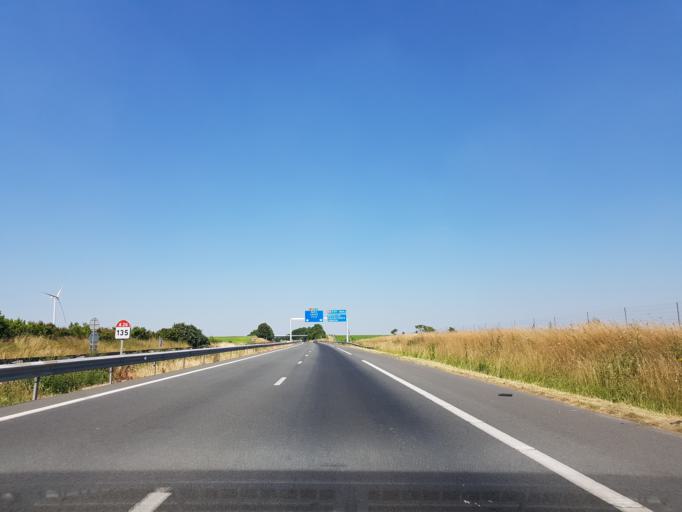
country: FR
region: Nord-Pas-de-Calais
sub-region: Departement du Nord
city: Marcoing
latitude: 50.1319
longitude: 3.1461
